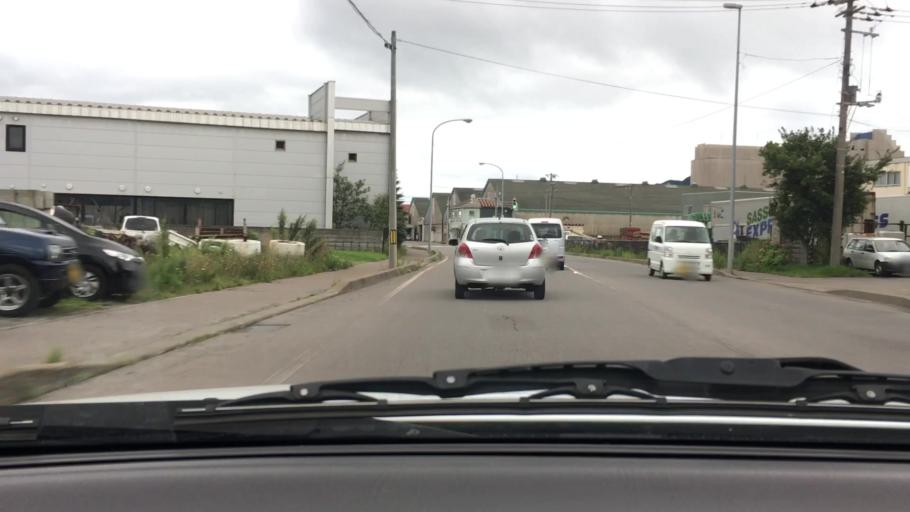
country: JP
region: Hokkaido
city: Hakodate
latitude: 41.7896
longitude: 140.7285
